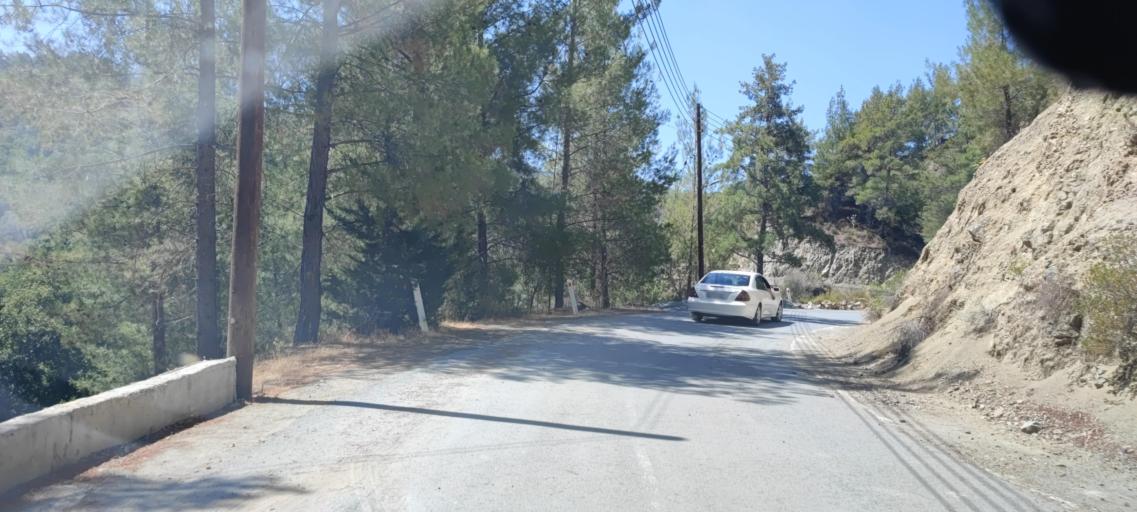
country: CY
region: Lefkosia
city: Kakopetria
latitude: 34.9293
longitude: 32.7939
